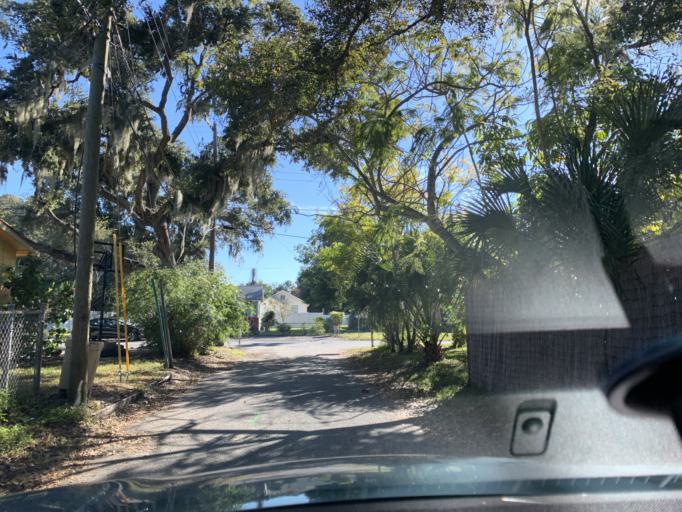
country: US
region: Florida
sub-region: Pinellas County
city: Gulfport
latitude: 27.7450
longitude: -82.7020
